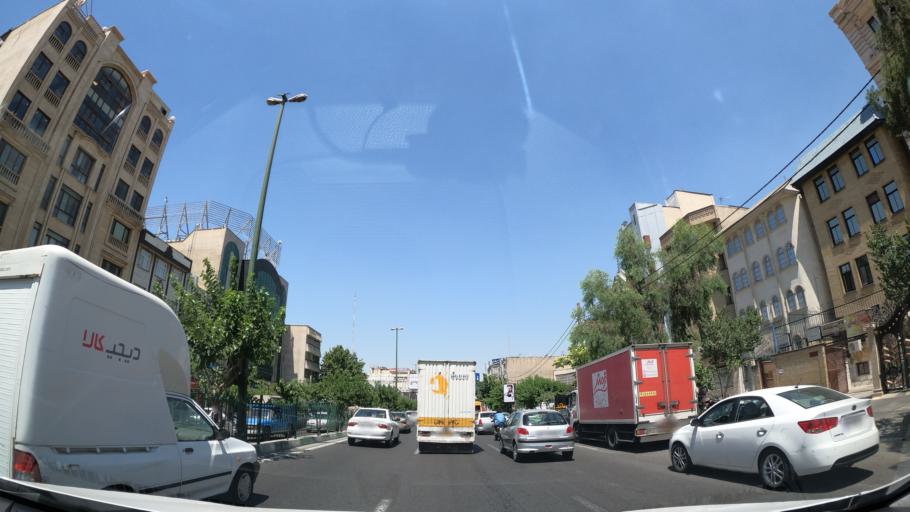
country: IR
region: Tehran
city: Tehran
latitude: 35.7271
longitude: 51.3746
